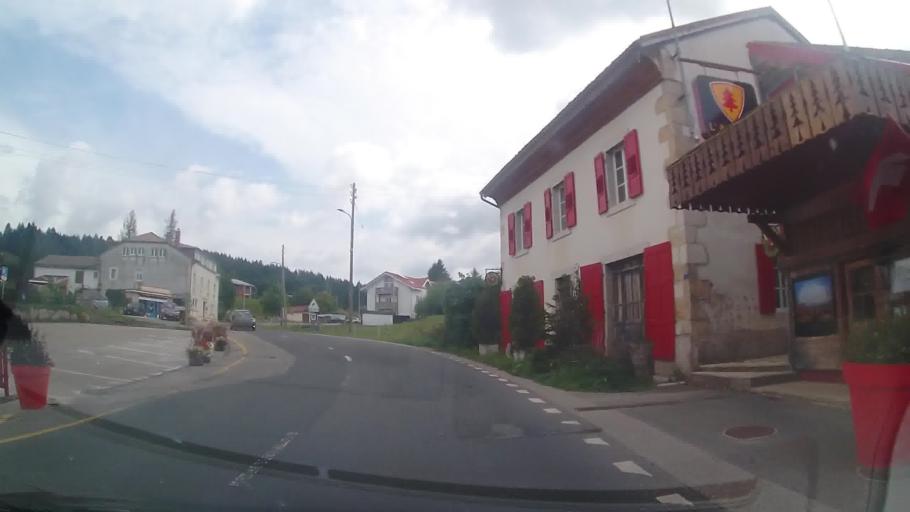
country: FR
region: Franche-Comte
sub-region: Departement du Jura
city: Les Rousses
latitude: 46.4647
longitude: 6.0731
